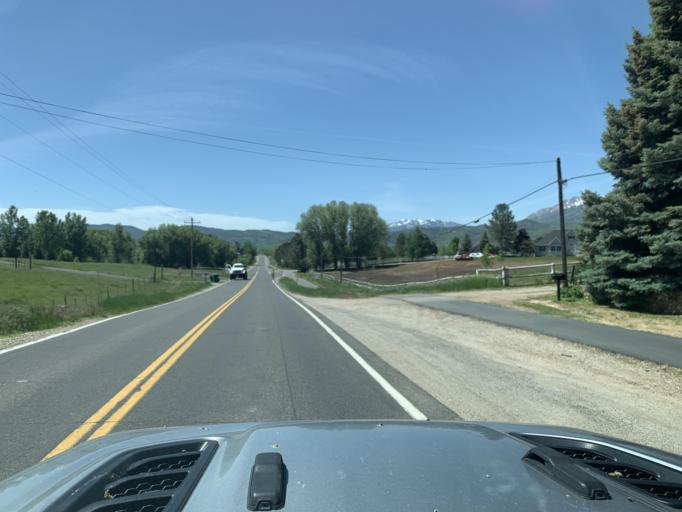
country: US
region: Utah
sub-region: Weber County
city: Wolf Creek
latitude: 41.2833
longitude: -111.7771
